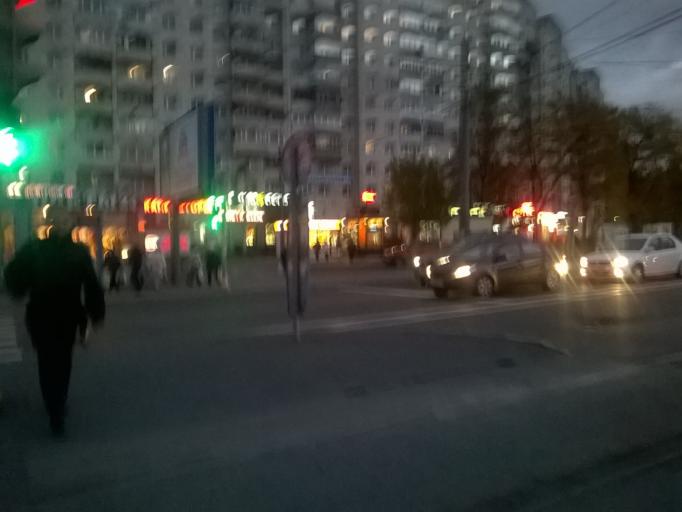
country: RU
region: St.-Petersburg
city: Ozerki
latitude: 60.0363
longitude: 30.3224
